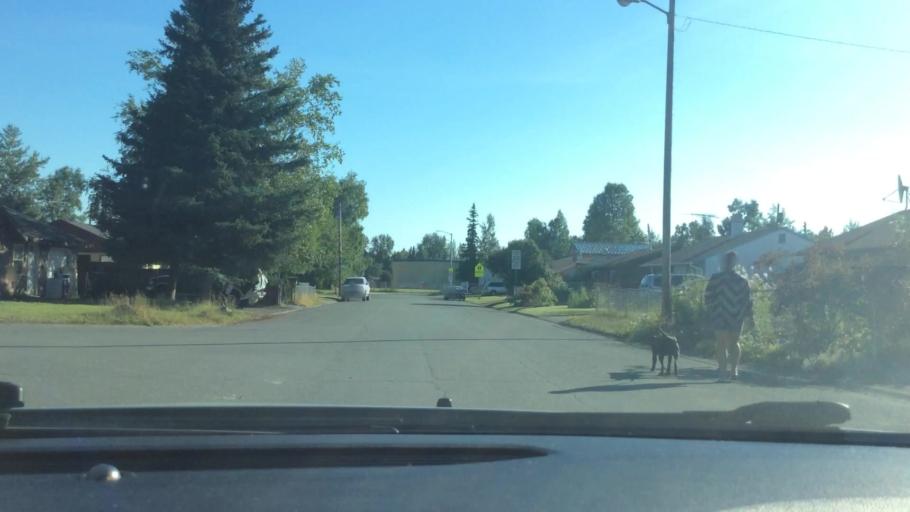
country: US
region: Alaska
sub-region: Anchorage Municipality
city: Anchorage
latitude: 61.2052
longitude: -149.7717
